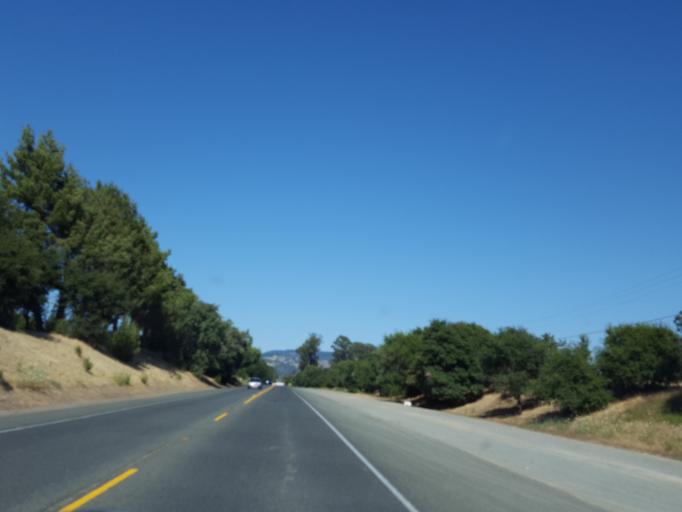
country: US
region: California
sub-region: Napa County
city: Napa
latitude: 38.2577
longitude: -122.3186
